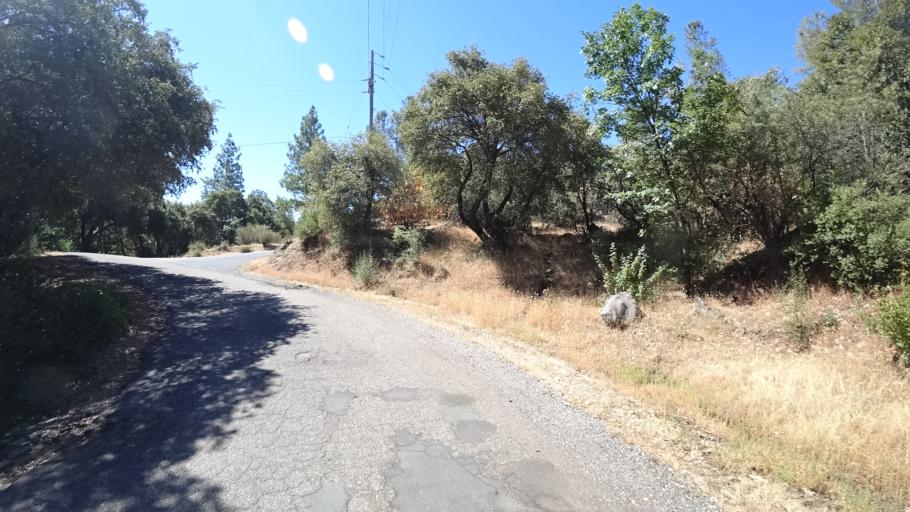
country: US
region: California
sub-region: Calaveras County
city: Forest Meadows
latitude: 38.1755
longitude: -120.3802
